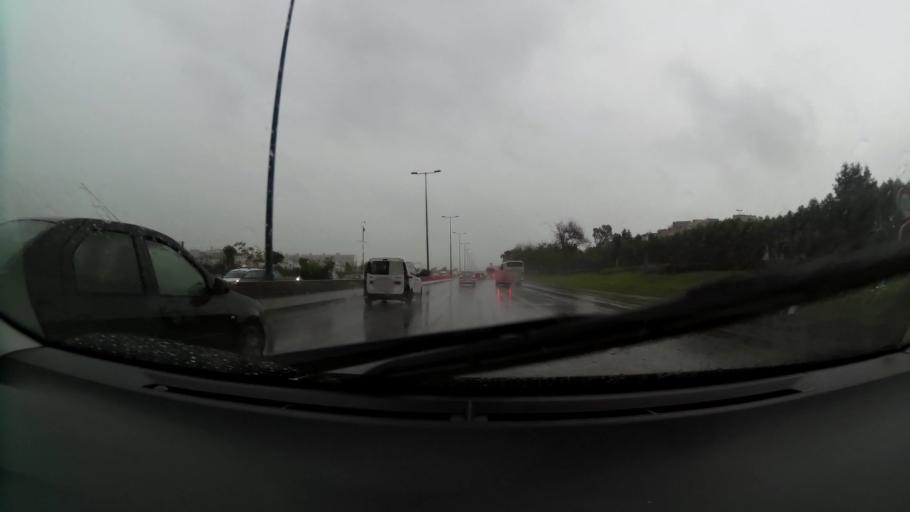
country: MA
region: Grand Casablanca
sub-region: Casablanca
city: Casablanca
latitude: 33.5766
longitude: -7.5592
